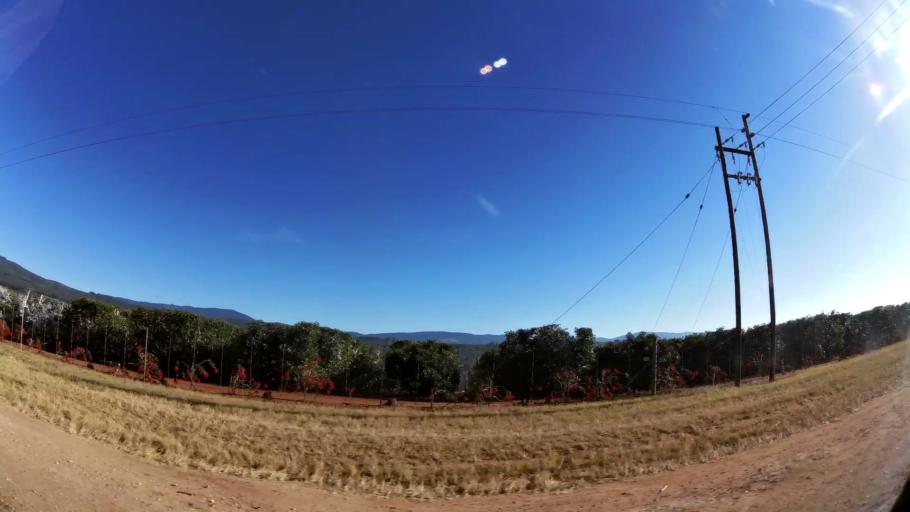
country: ZA
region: Limpopo
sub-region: Mopani District Municipality
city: Tzaneen
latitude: -23.8470
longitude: 30.1211
